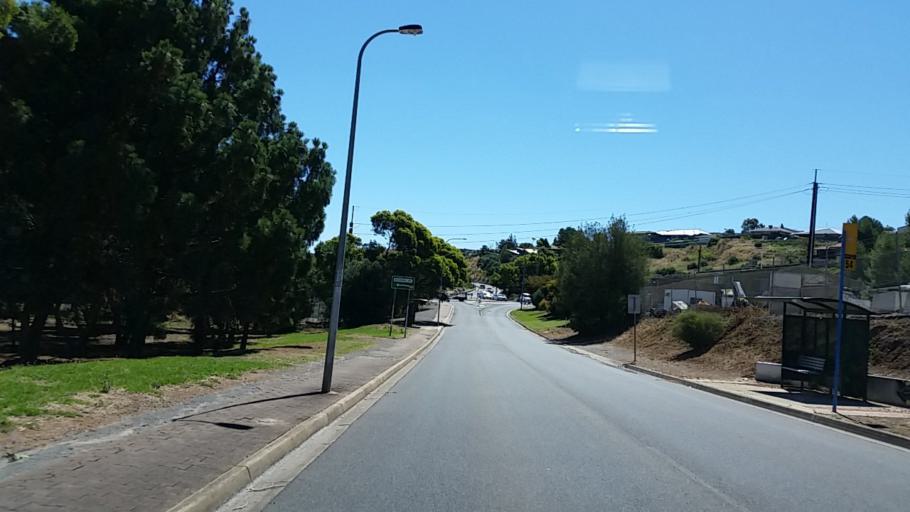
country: AU
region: South Australia
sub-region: Marion
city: Happy Valley
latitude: -35.0766
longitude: 138.5291
